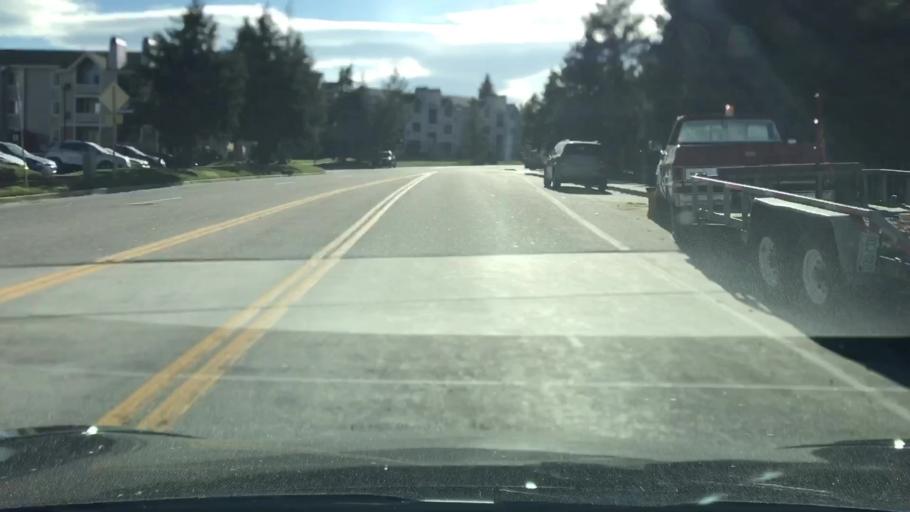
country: US
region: Colorado
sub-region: Arapahoe County
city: Glendale
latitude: 39.6684
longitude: -104.8921
